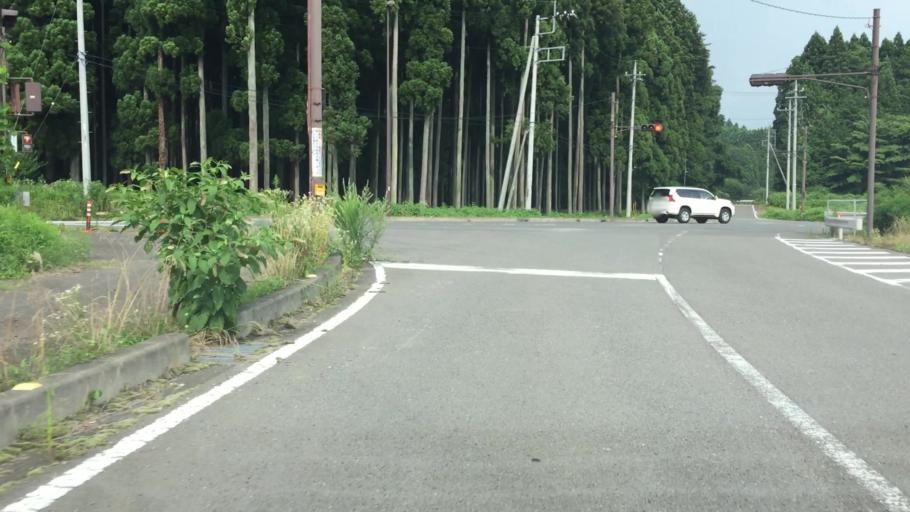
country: JP
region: Tochigi
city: Kuroiso
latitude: 36.9621
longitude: 139.9849
